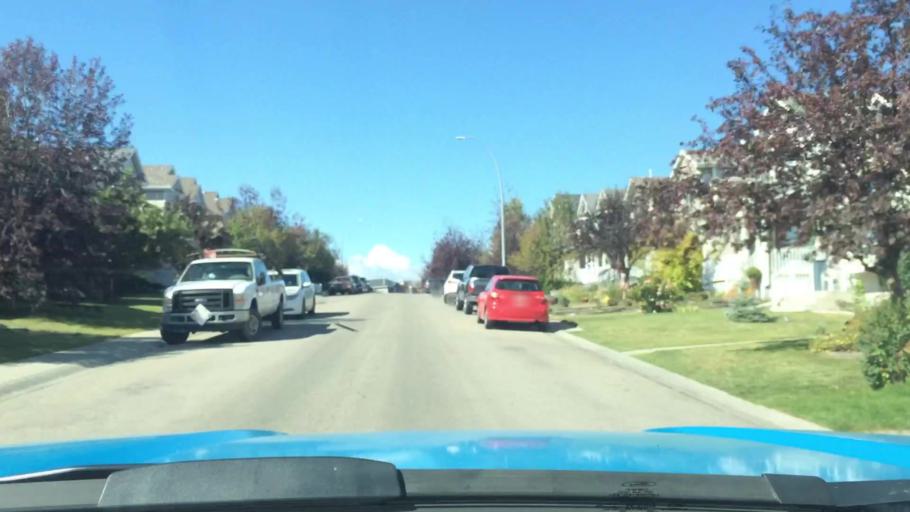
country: CA
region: Alberta
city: Calgary
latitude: 50.9030
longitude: -114.1059
